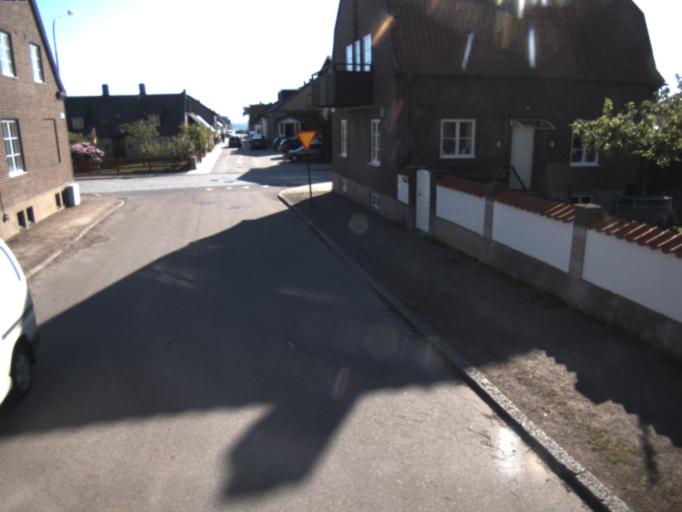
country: SE
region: Skane
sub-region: Helsingborg
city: Rydeback
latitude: 56.0015
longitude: 12.7378
